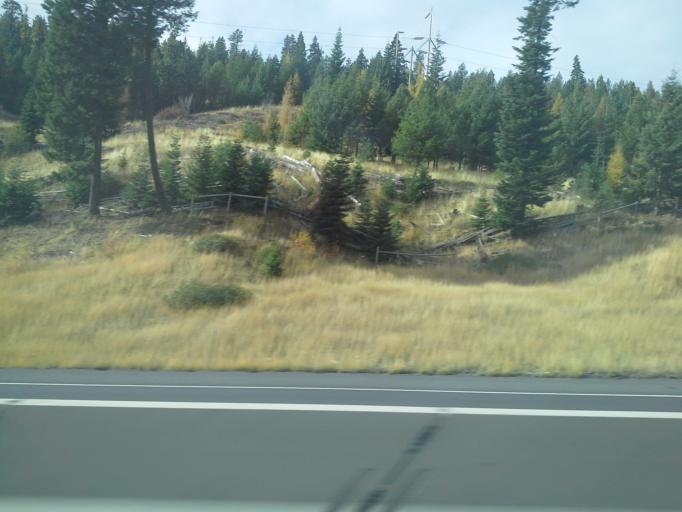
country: US
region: Oregon
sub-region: Union County
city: La Grande
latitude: 45.4088
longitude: -118.3418
